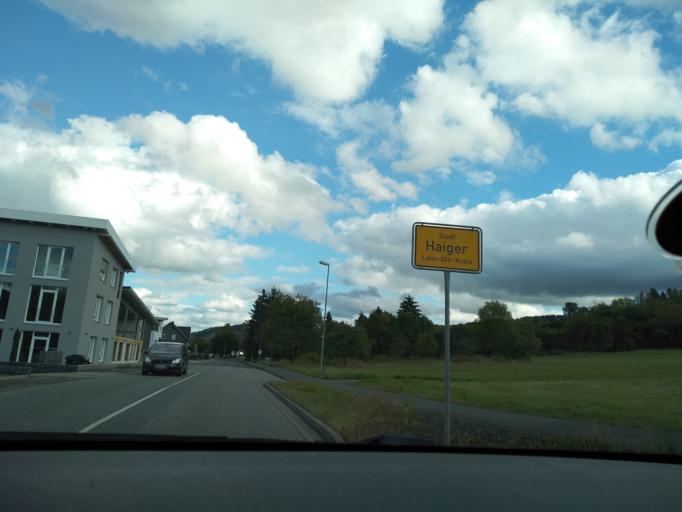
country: DE
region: Hesse
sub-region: Regierungsbezirk Giessen
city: Haiger
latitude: 50.7453
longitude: 8.1922
